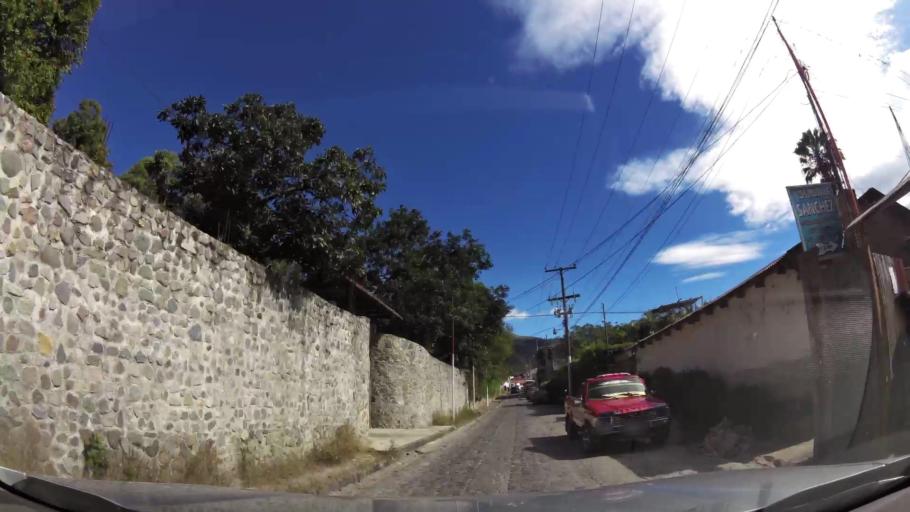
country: GT
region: Solola
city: Panajachel
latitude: 14.7425
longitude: -91.1602
